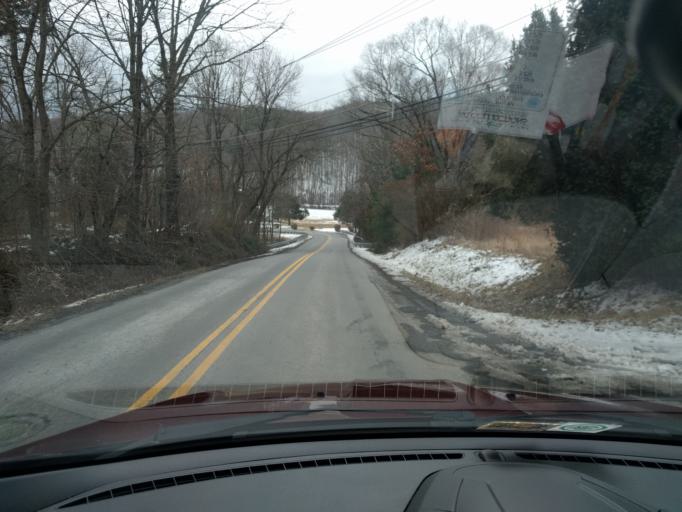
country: US
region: Virginia
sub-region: Alleghany County
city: Clifton Forge
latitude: 37.8253
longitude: -79.7933
